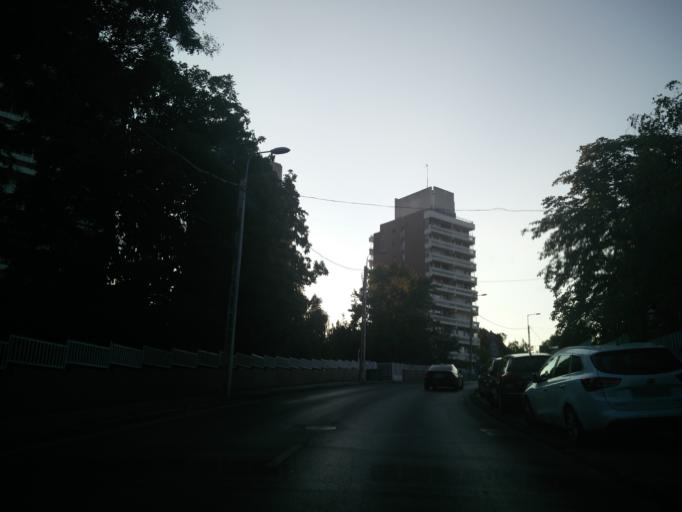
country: HU
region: Budapest
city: Budapest XII. keruelet
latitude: 47.5018
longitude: 19.0065
